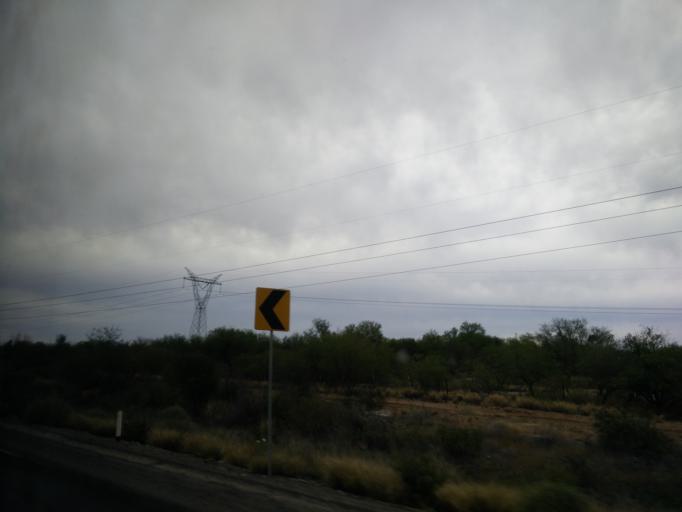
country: MX
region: Sonora
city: Hermosillo
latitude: 28.6651
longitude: -110.9971
